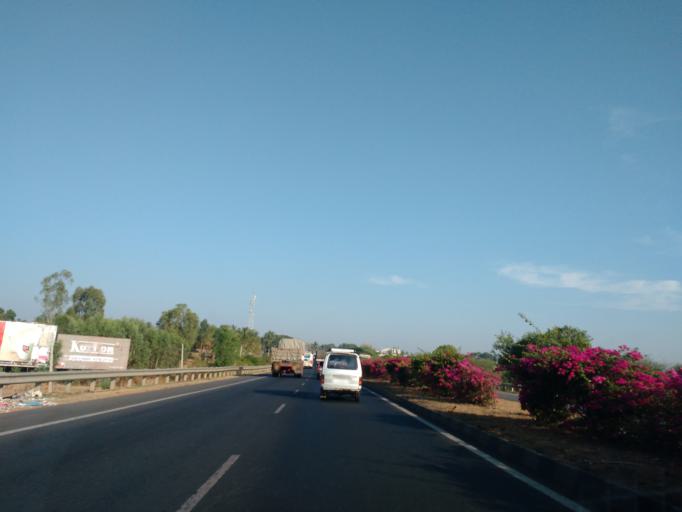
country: IN
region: Karnataka
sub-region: Bangalore Rural
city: Nelamangala
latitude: 13.1739
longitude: 77.3027
